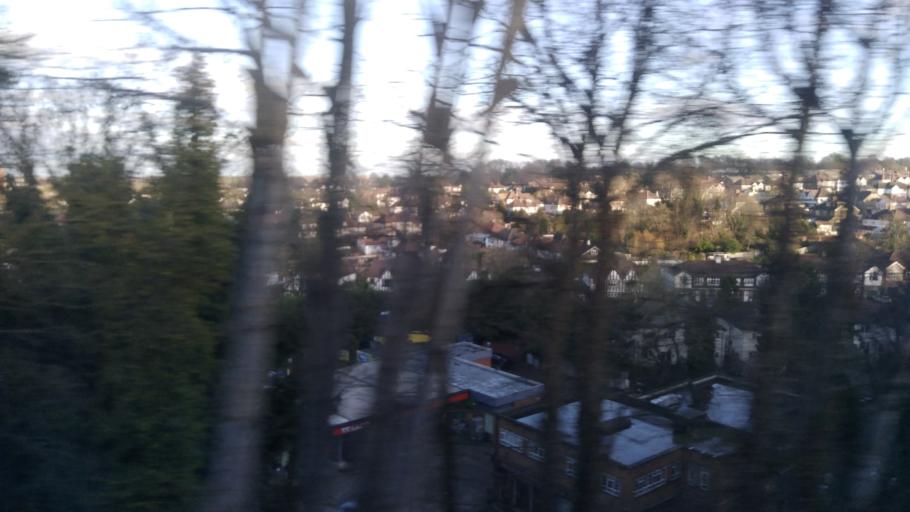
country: GB
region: England
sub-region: Greater London
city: Orpington
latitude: 51.3664
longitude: 0.0947
